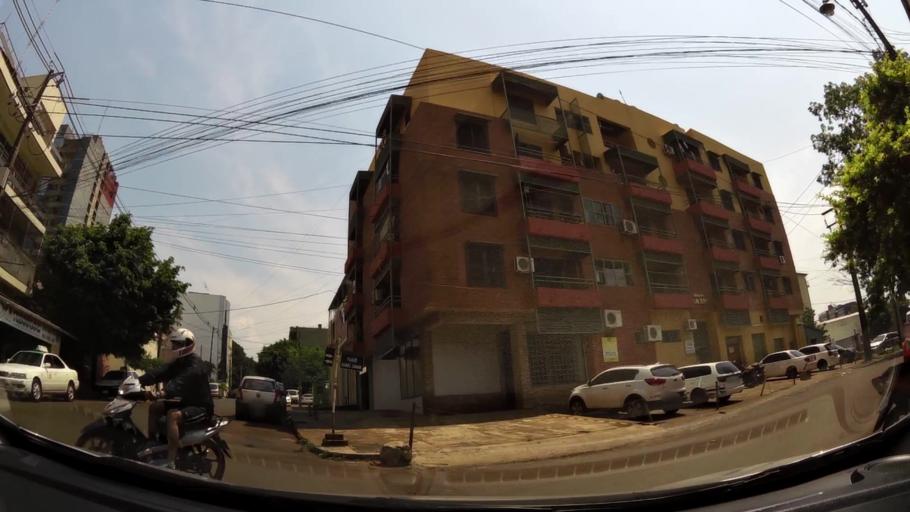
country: PY
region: Alto Parana
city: Ciudad del Este
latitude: -25.5172
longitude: -54.6104
